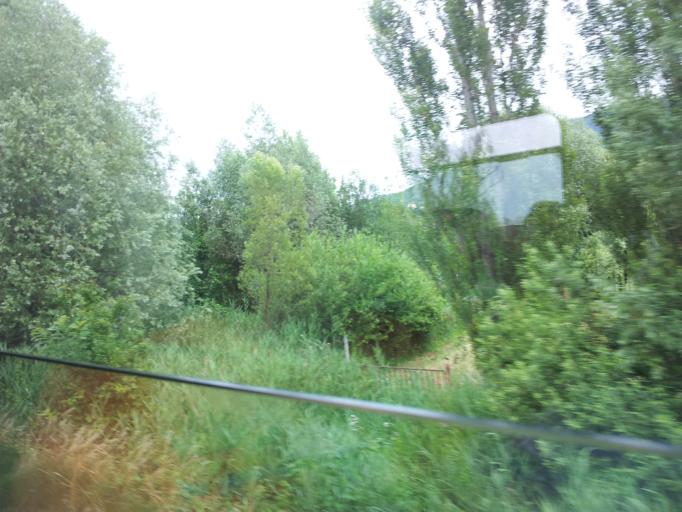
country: HU
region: Veszprem
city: Badacsonytomaj
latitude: 46.7951
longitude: 17.4702
